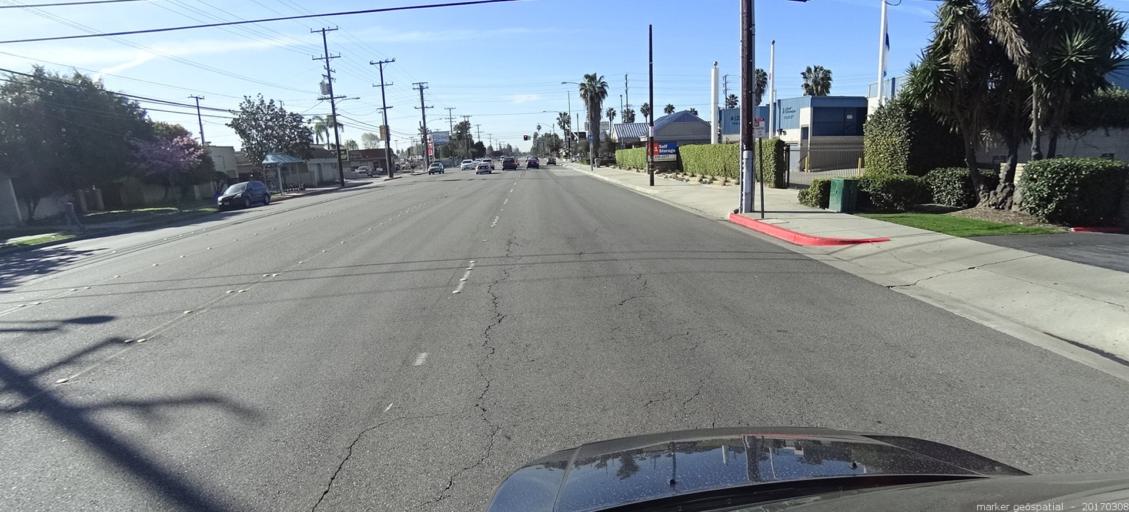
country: US
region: California
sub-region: Orange County
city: Stanton
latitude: 33.8185
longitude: -118.0109
